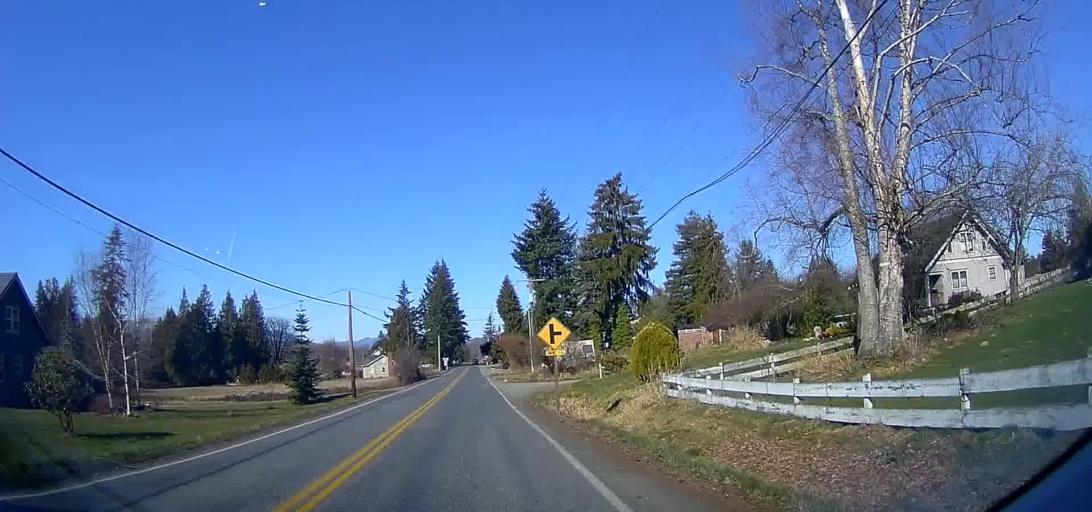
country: US
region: Washington
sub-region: Skagit County
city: Burlington
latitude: 48.4520
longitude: -122.3027
